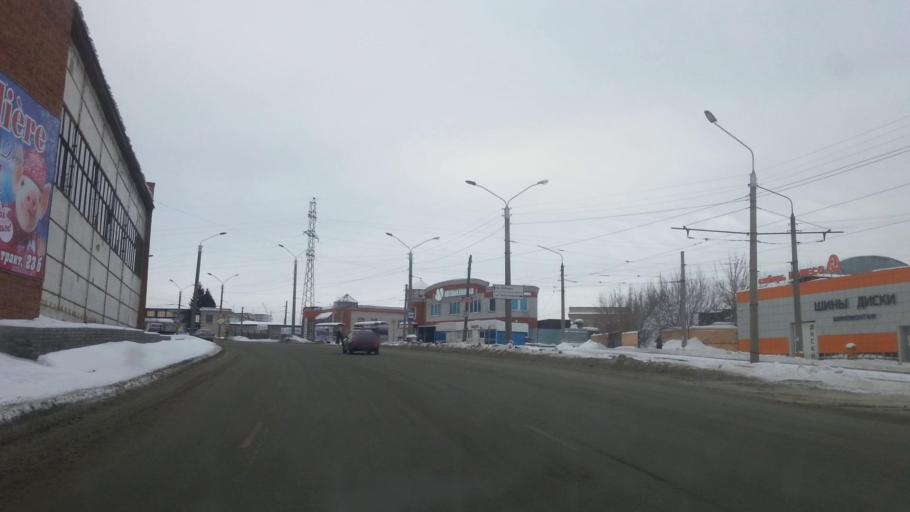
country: RU
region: Altai Krai
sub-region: Gorod Barnaulskiy
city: Barnaul
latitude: 53.3394
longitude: 83.7433
